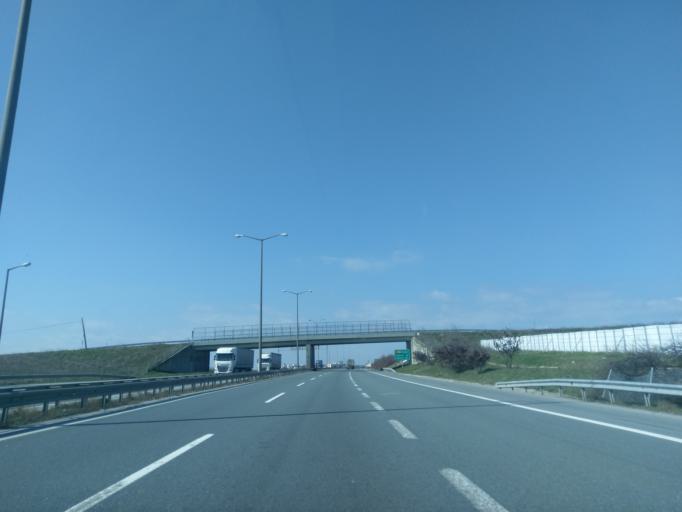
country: TR
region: Istanbul
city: Selimpasa
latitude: 41.0711
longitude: 28.3823
